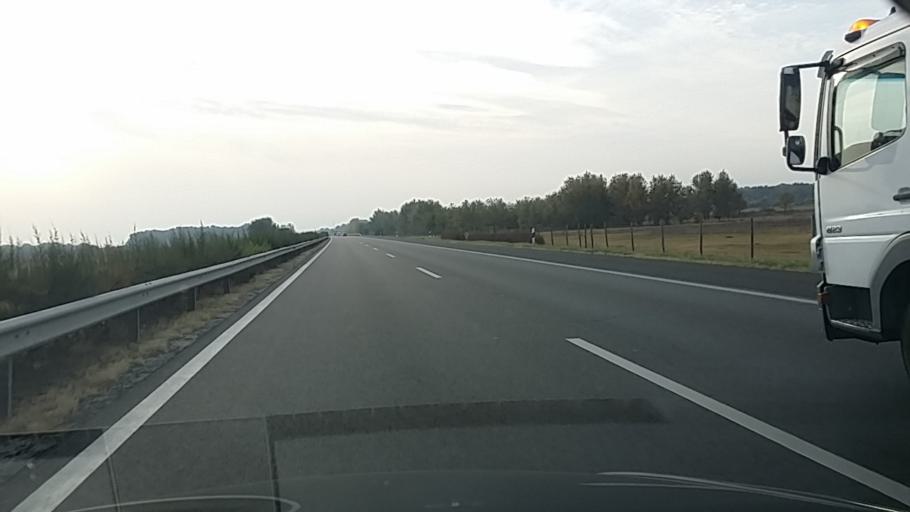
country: HU
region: Csongrad
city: Balastya
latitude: 46.4228
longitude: 19.9530
